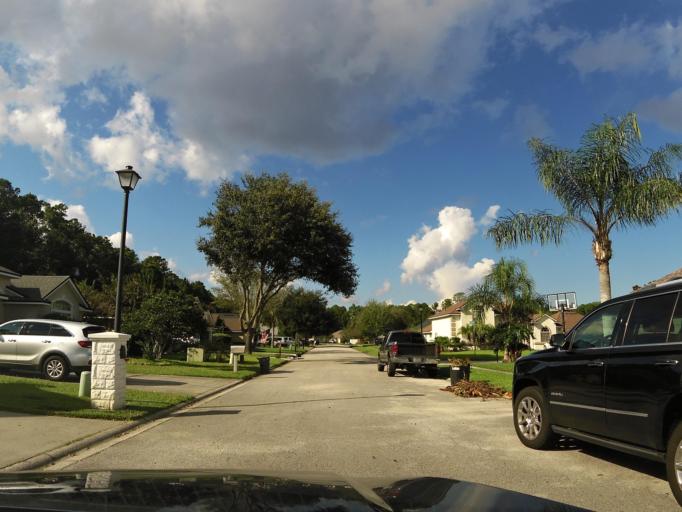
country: US
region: Florida
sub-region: Duval County
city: Jacksonville Beach
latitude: 30.2775
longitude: -81.4991
